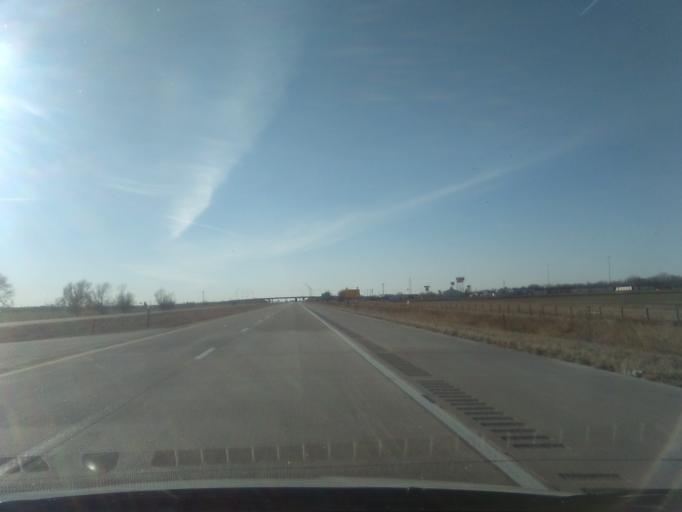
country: US
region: Colorado
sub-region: Sedgwick County
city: Julesburg
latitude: 41.0522
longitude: -102.0603
